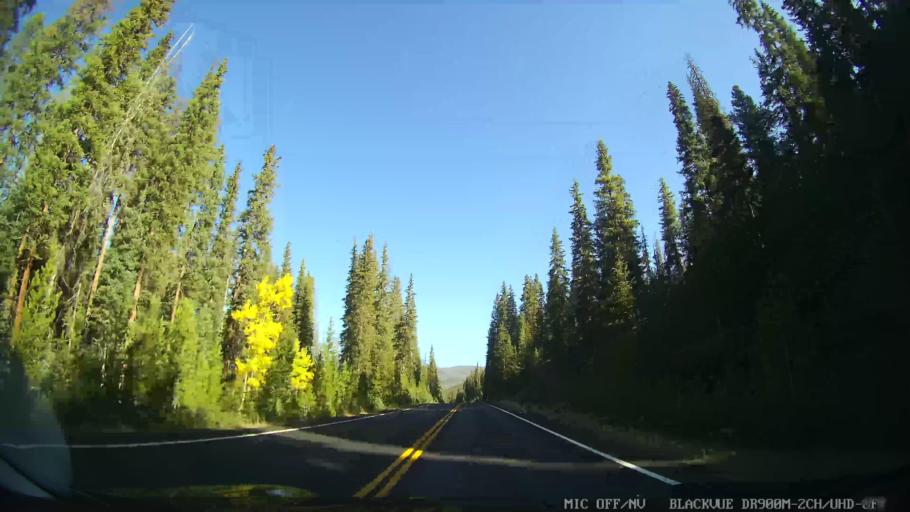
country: US
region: Colorado
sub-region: Grand County
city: Granby
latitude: 40.3010
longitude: -105.8431
